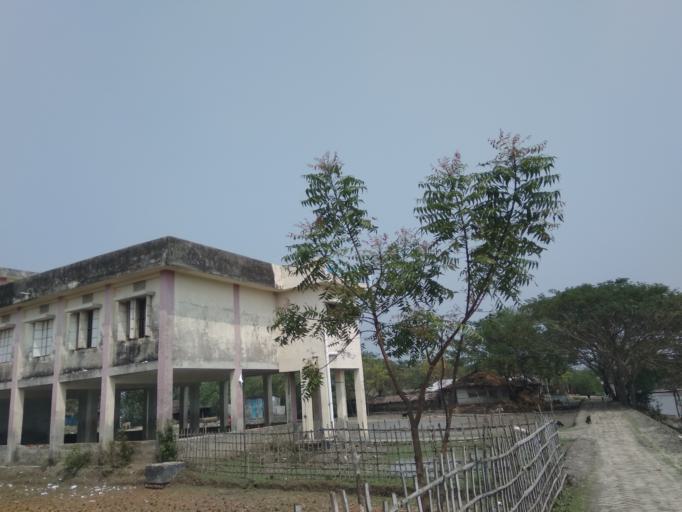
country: IN
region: West Bengal
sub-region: North 24 Parganas
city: Taki
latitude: 22.2594
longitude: 89.2591
